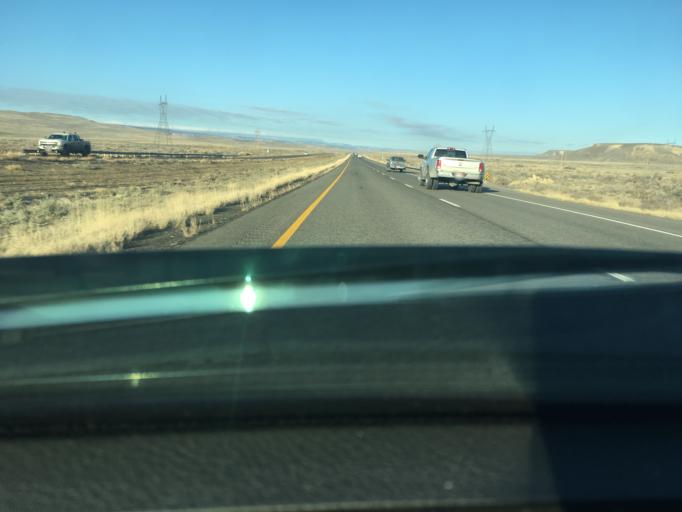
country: US
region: Colorado
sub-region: Delta County
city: Delta
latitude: 38.7590
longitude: -108.1880
